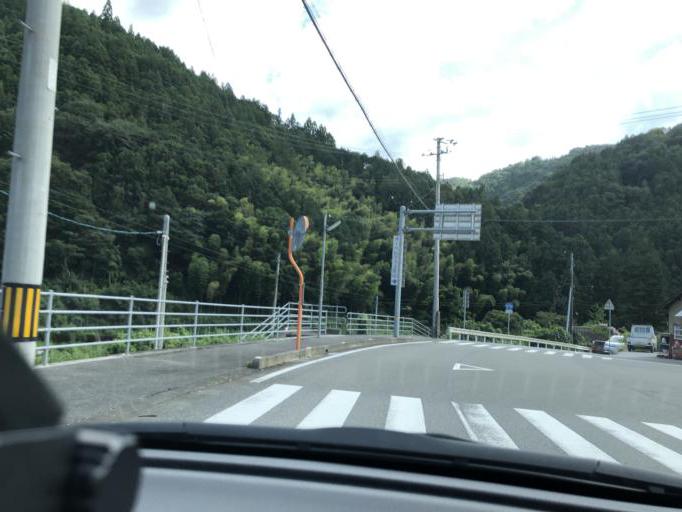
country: JP
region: Kochi
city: Kochi-shi
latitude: 33.6232
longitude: 133.4980
